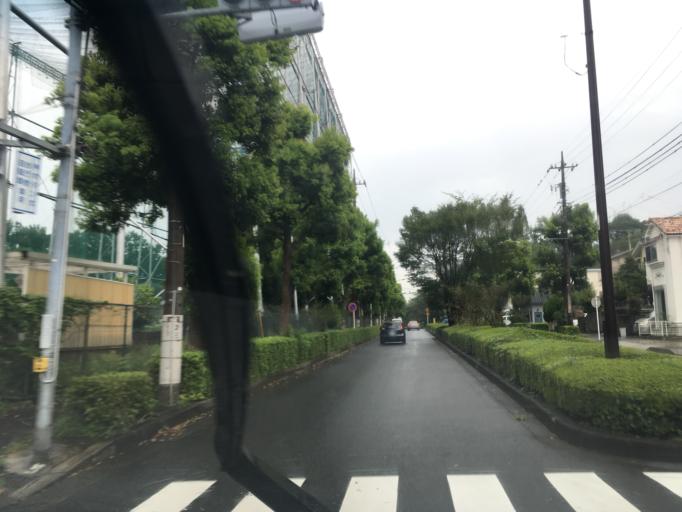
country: JP
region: Tokyo
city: Hino
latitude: 35.6074
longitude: 139.4269
